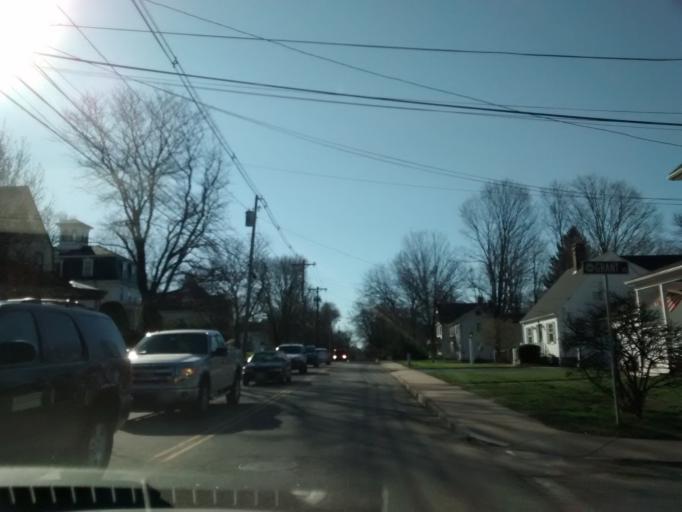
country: US
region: Massachusetts
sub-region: Worcester County
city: Westborough
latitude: 42.2710
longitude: -71.6210
